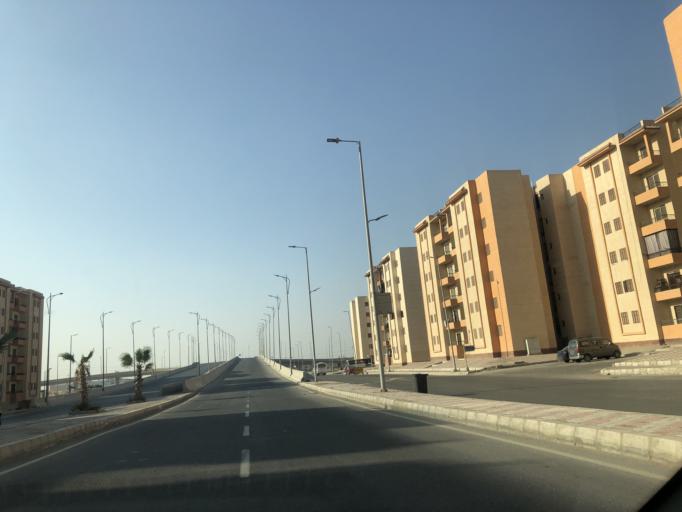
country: EG
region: Al Jizah
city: Madinat Sittah Uktubar
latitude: 29.8907
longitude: 30.8971
